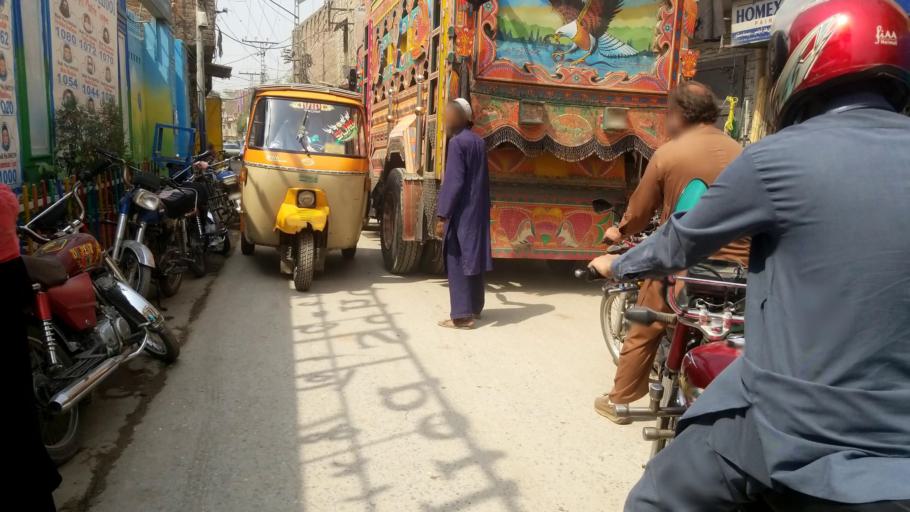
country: PK
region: Khyber Pakhtunkhwa
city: Peshawar
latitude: 33.9842
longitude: 71.5345
